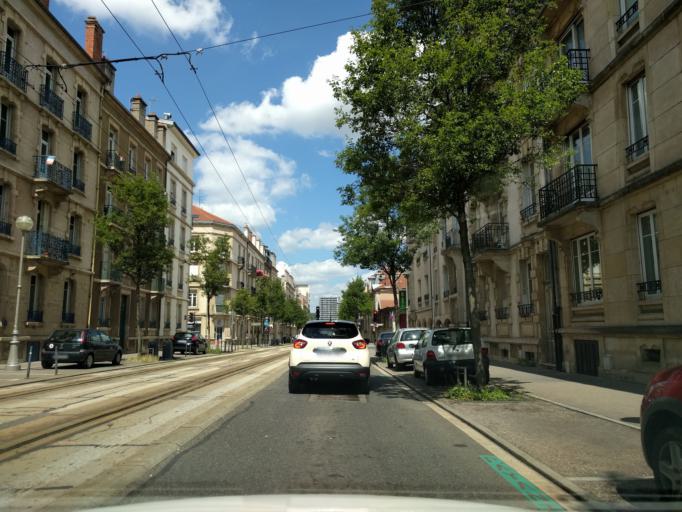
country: FR
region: Lorraine
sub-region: Departement de Meurthe-et-Moselle
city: Nancy
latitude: 48.6817
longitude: 6.1782
